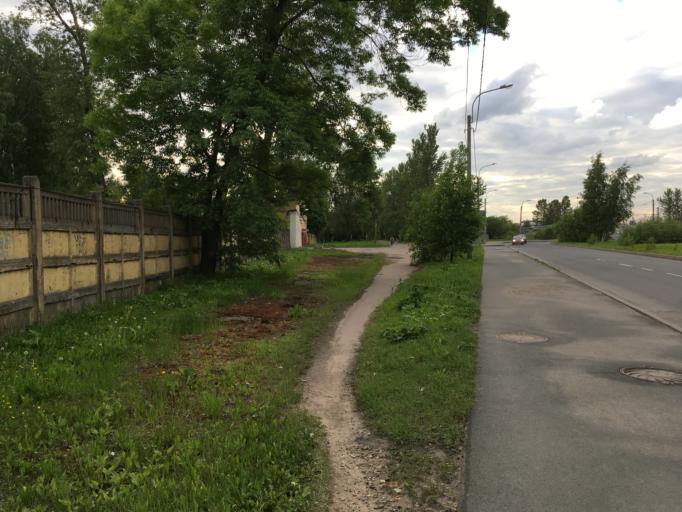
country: RU
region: St.-Petersburg
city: Centralniy
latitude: 59.9043
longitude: 30.3747
